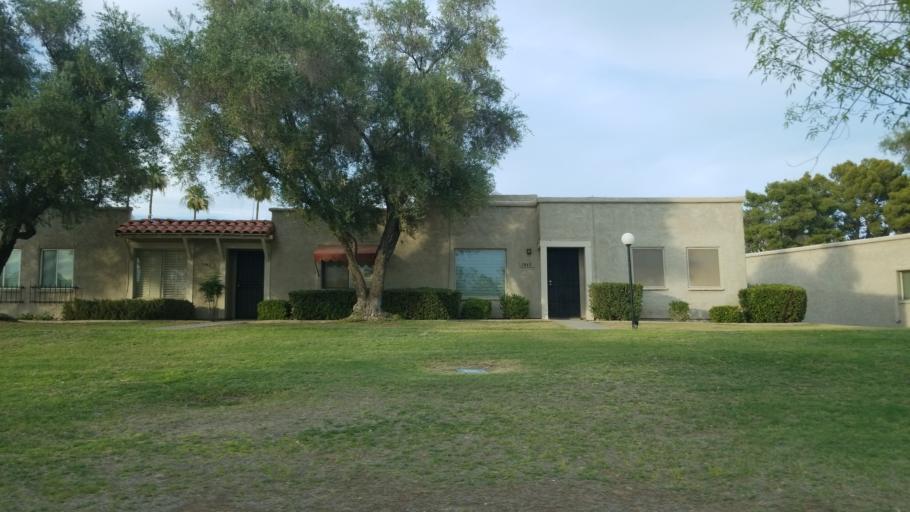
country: US
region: Arizona
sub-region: Maricopa County
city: Scottsdale
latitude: 33.5105
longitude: -111.9064
